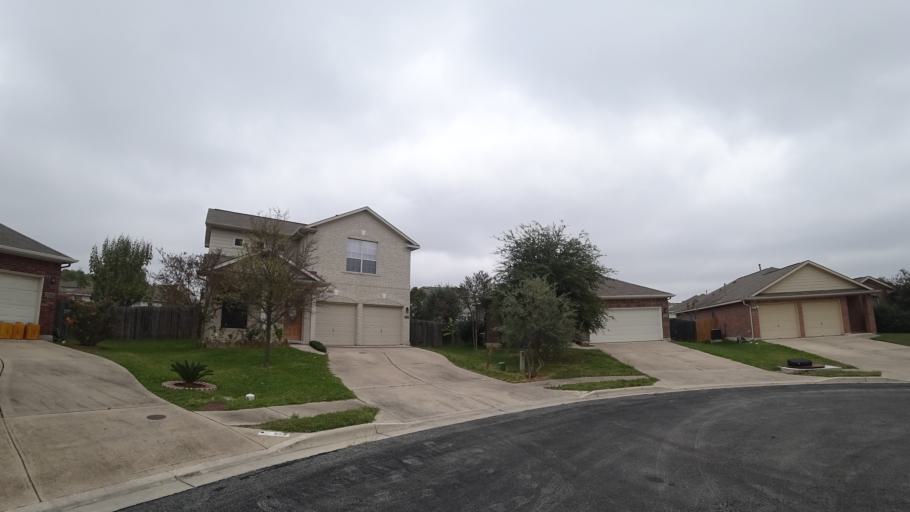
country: US
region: Texas
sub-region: Travis County
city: Pflugerville
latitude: 30.3756
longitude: -97.6525
